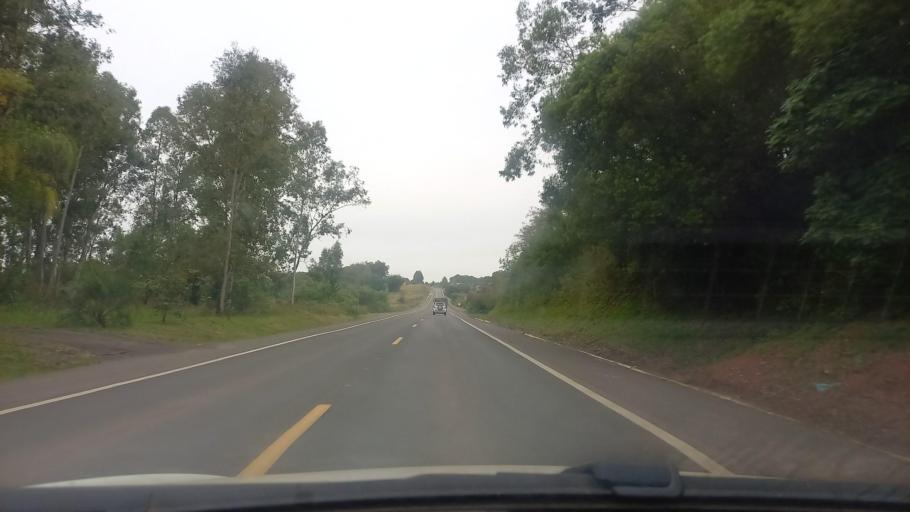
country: BR
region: Rio Grande do Sul
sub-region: Rosario Do Sul
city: Rosario do Sul
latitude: -30.2626
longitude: -54.9690
